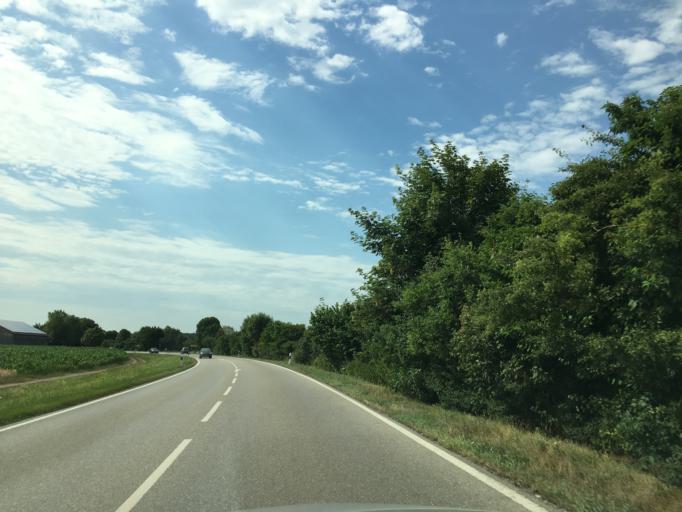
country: DE
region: Bavaria
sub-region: Upper Bavaria
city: Erding
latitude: 48.2767
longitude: 11.9176
